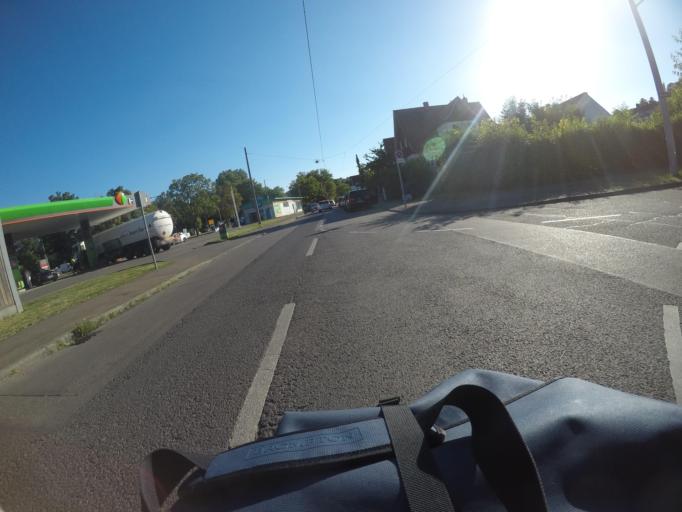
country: DE
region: Baden-Wuerttemberg
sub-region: Regierungsbezirk Stuttgart
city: Stuttgart Muehlhausen
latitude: 48.8406
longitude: 9.2266
